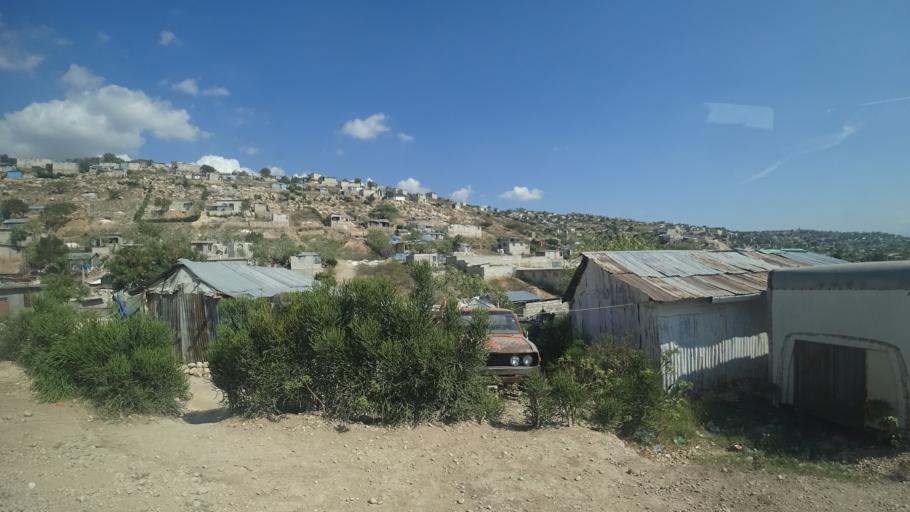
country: HT
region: Ouest
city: Croix des Bouquets
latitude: 18.6603
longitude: -72.2858
